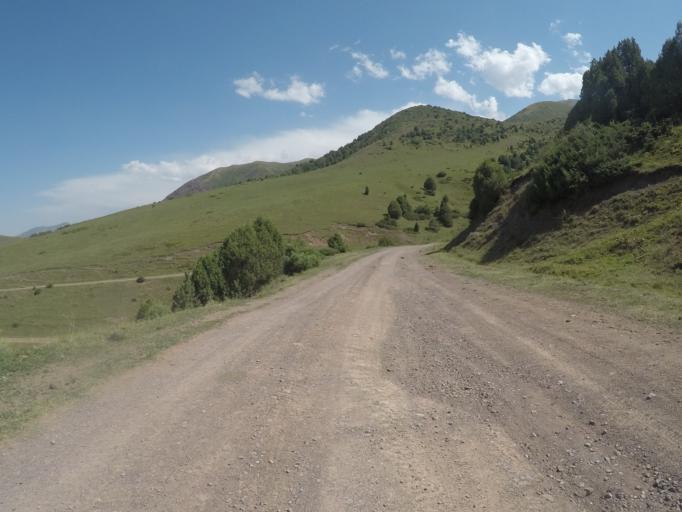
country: KG
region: Chuy
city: Bishkek
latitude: 42.6465
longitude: 74.5622
